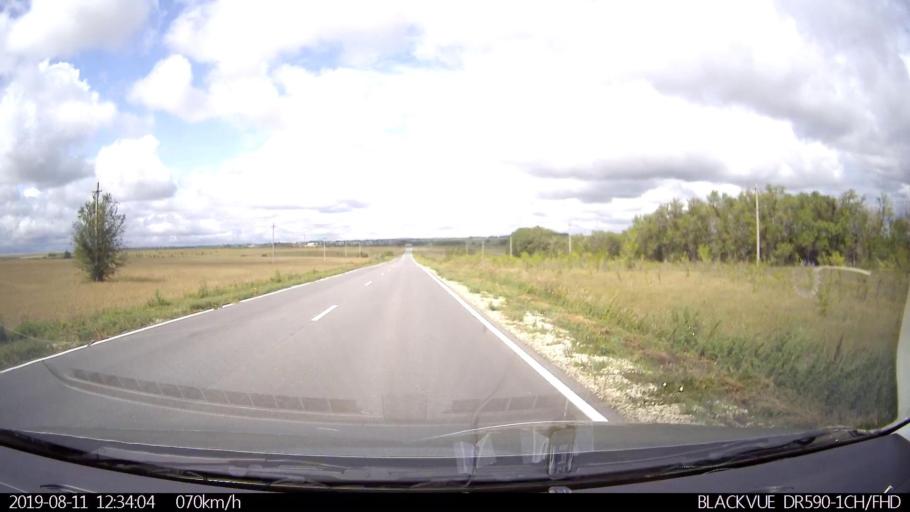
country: RU
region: Ulyanovsk
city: Ignatovka
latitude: 53.8142
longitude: 47.8476
